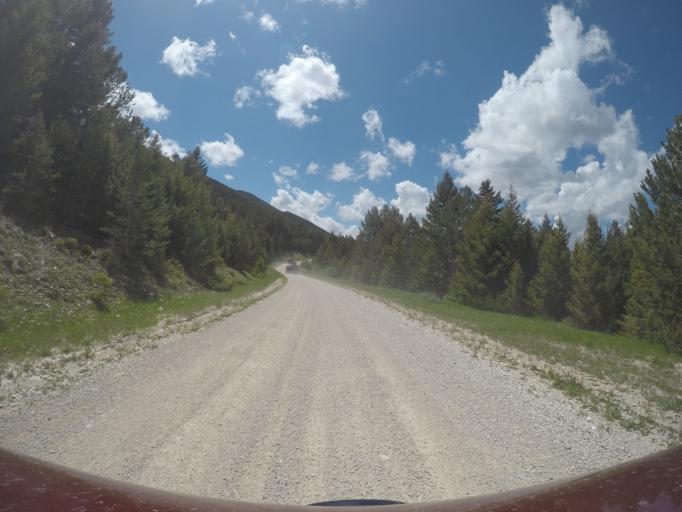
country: US
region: Wyoming
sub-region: Big Horn County
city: Lovell
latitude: 45.2045
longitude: -108.5259
